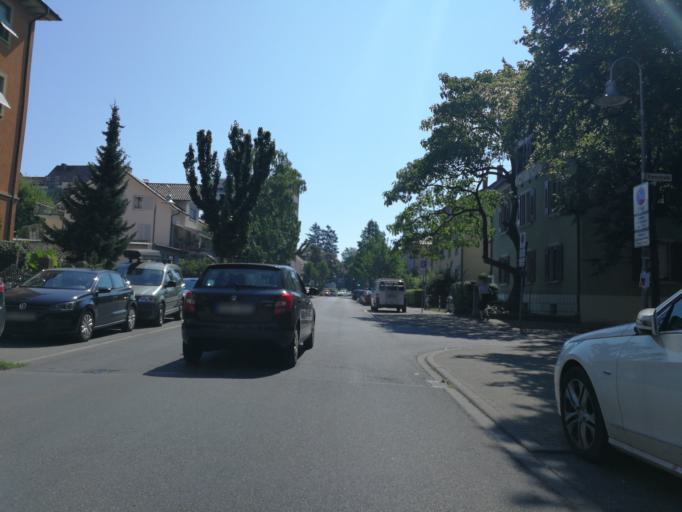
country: DE
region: Baden-Wuerttemberg
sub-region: Freiburg Region
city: Konstanz
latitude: 47.6621
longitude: 9.1680
